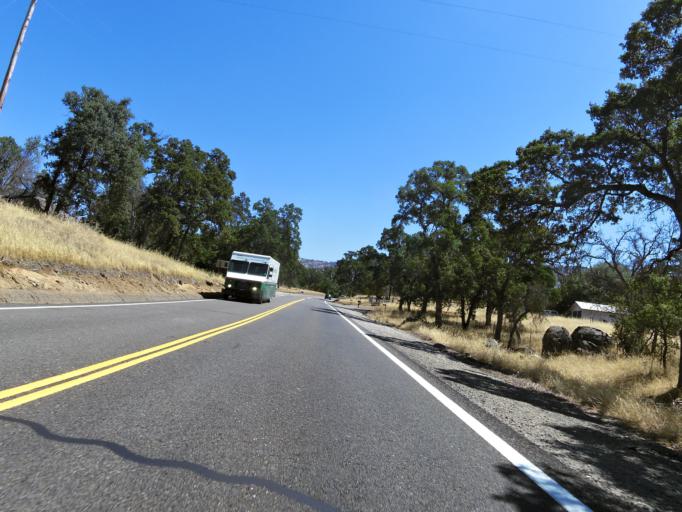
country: US
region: California
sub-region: Mariposa County
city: Mariposa
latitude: 37.4392
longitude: -120.0854
